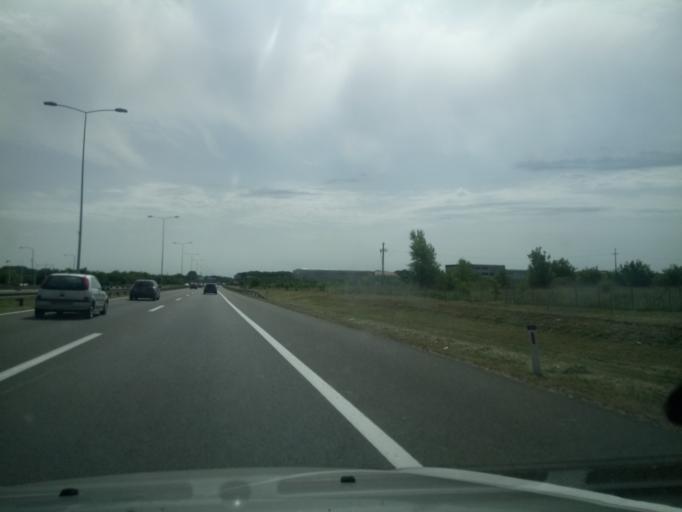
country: RS
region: Central Serbia
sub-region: Belgrade
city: Surcin
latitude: 44.8344
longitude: 20.3177
